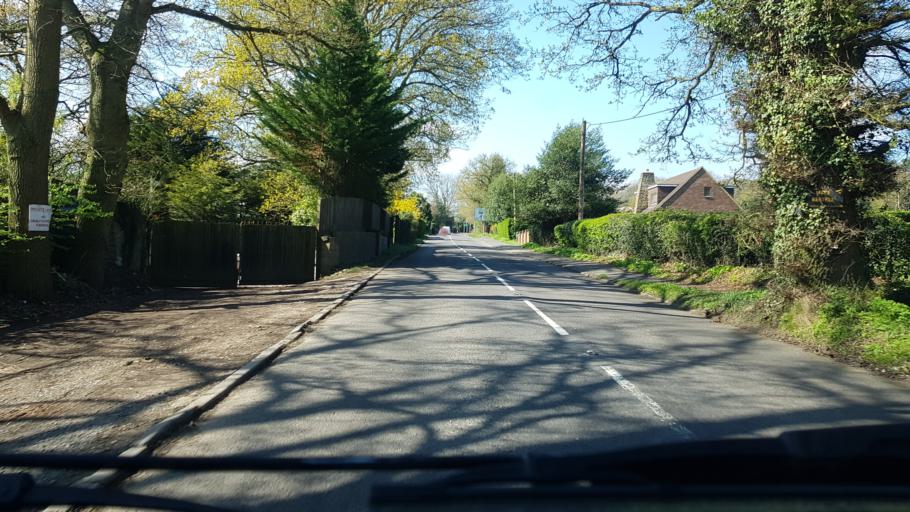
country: GB
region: England
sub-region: Surrey
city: Normandy
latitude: 51.2550
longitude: -0.6939
